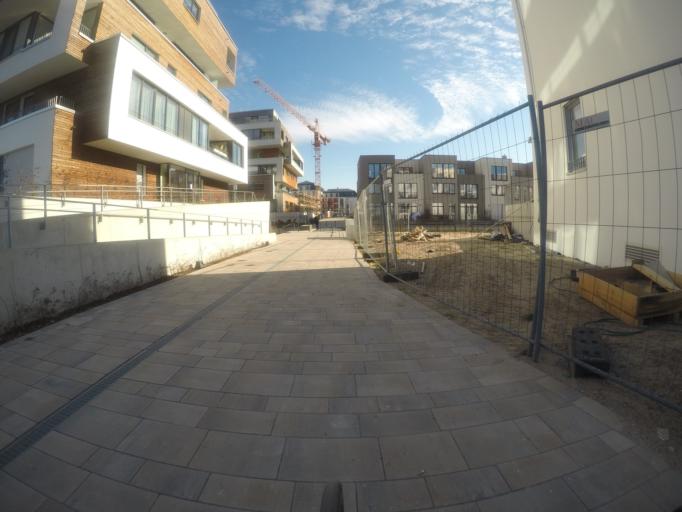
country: DE
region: Berlin
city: Grunau
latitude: 52.4260
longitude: 13.5772
